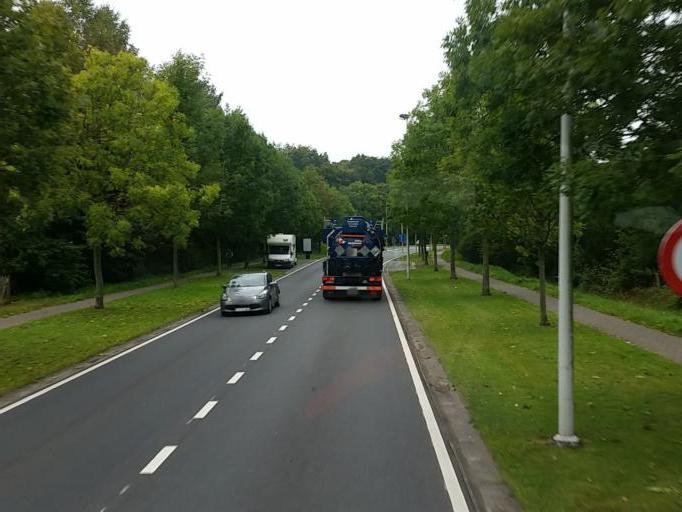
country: BE
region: Flanders
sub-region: Provincie Antwerpen
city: Schoten
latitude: 51.2505
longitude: 4.4787
